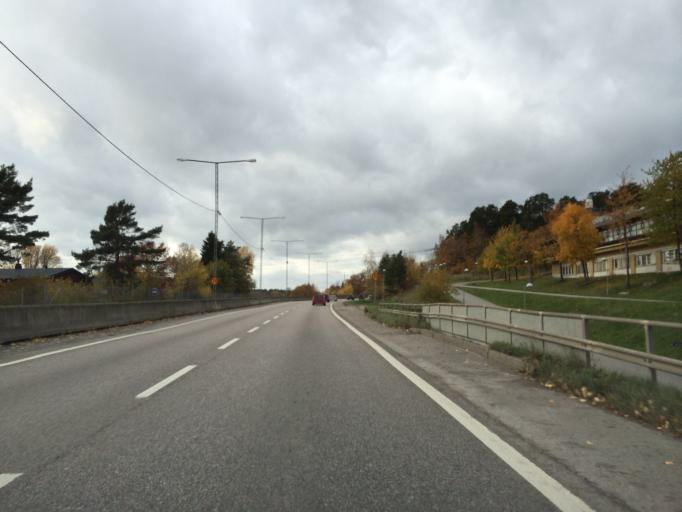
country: SE
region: Stockholm
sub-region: Stockholms Kommun
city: Bromma
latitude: 59.3720
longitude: 17.9351
